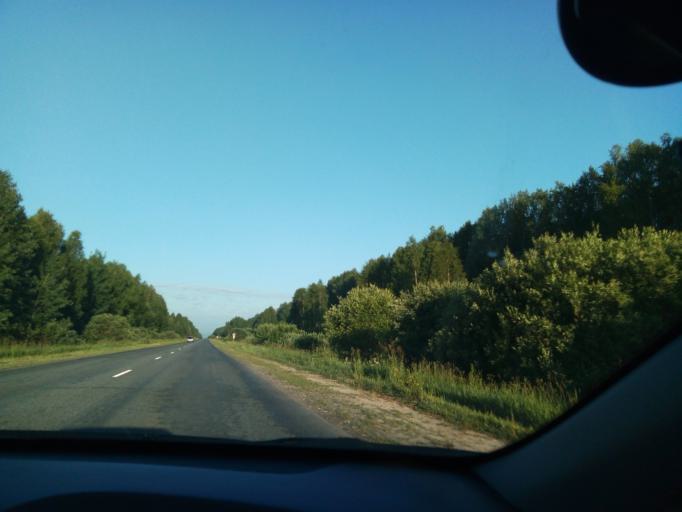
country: RU
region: Nizjnij Novgorod
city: Satis
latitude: 54.8975
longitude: 43.1192
